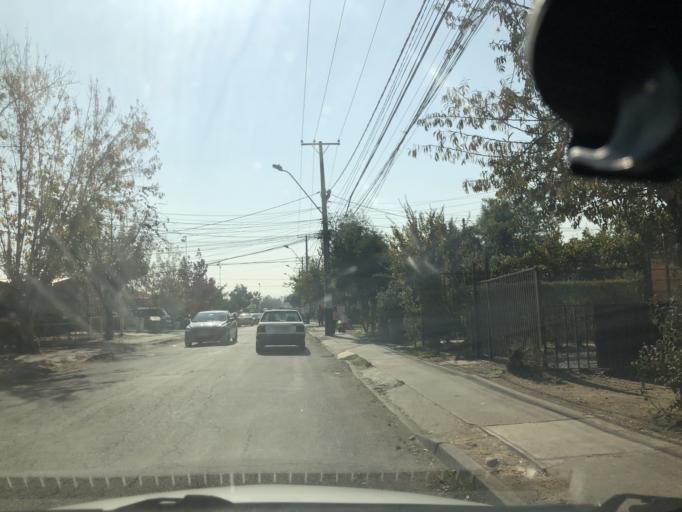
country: CL
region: Santiago Metropolitan
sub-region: Provincia de Cordillera
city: Puente Alto
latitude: -33.5996
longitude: -70.5584
